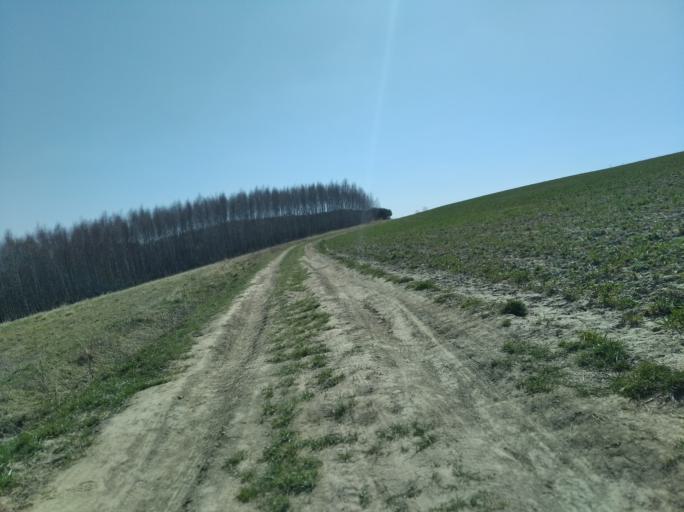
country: PL
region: Subcarpathian Voivodeship
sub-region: Powiat strzyzowski
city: Polomia
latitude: 49.8822
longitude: 21.8555
